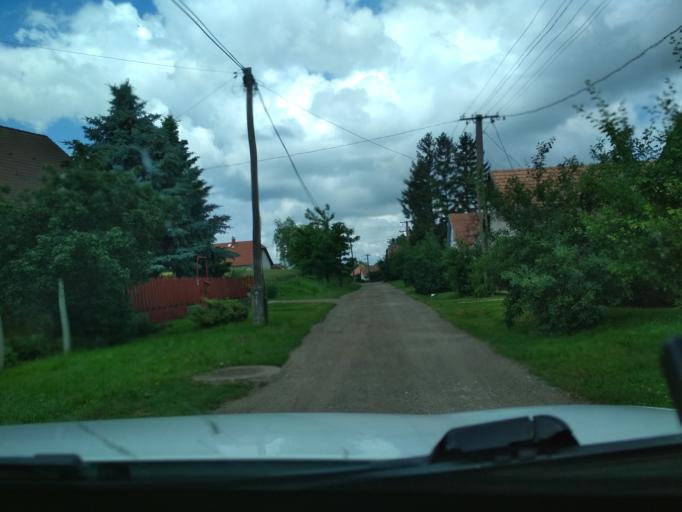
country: HU
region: Jasz-Nagykun-Szolnok
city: Tiszafured
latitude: 47.6106
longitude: 20.7463
